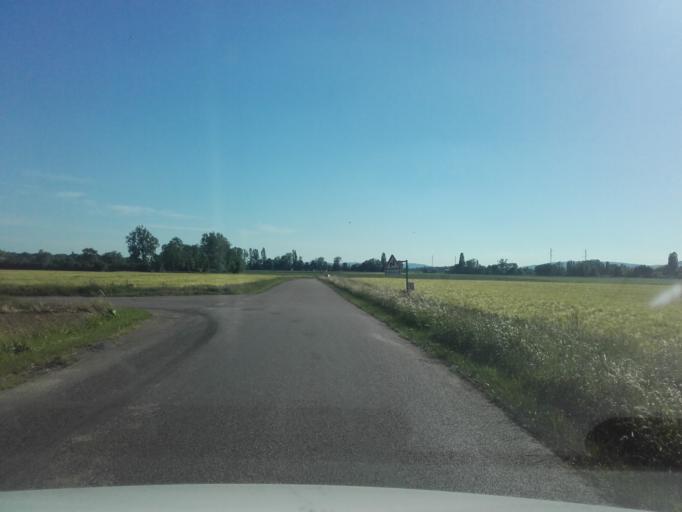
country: FR
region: Bourgogne
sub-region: Departement de la Cote-d'Or
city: Bligny-les-Beaune
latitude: 46.9886
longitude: 4.8421
